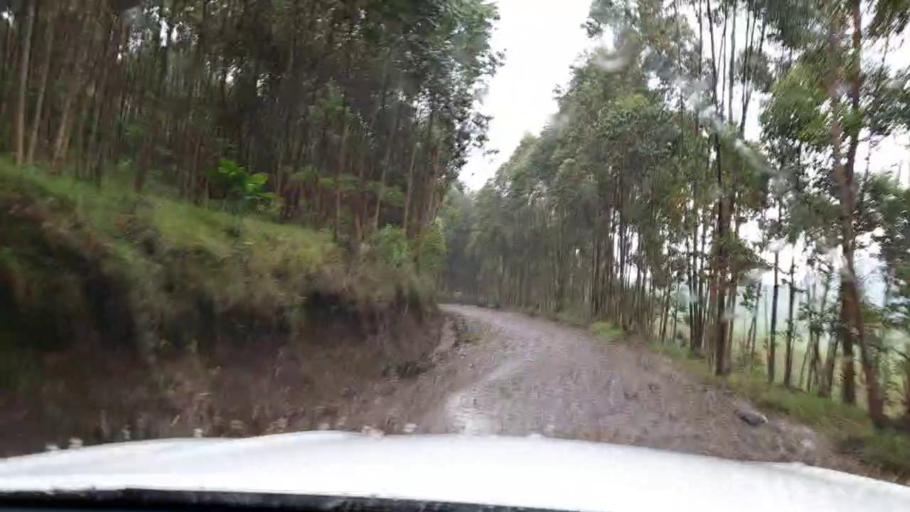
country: RW
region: Western Province
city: Cyangugu
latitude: -2.4692
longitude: 29.0340
